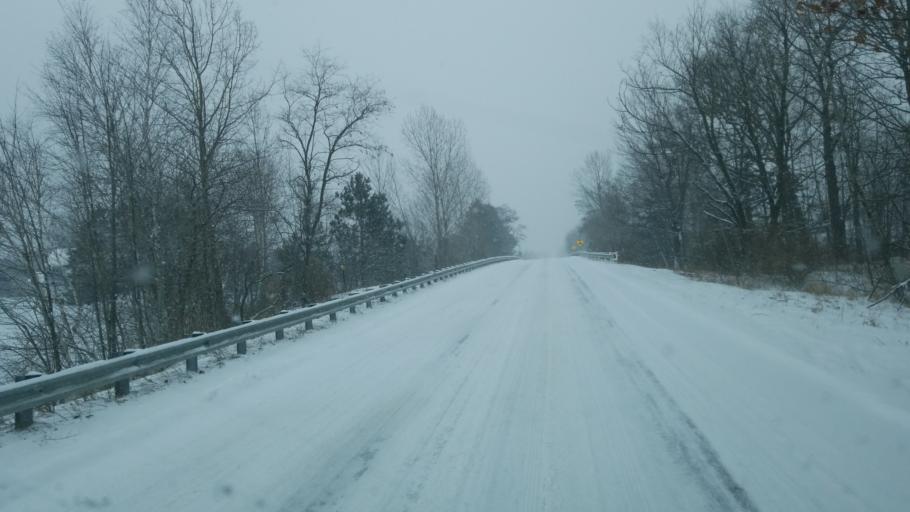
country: US
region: Michigan
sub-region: Mecosta County
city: Canadian Lakes
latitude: 43.5905
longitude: -85.2896
